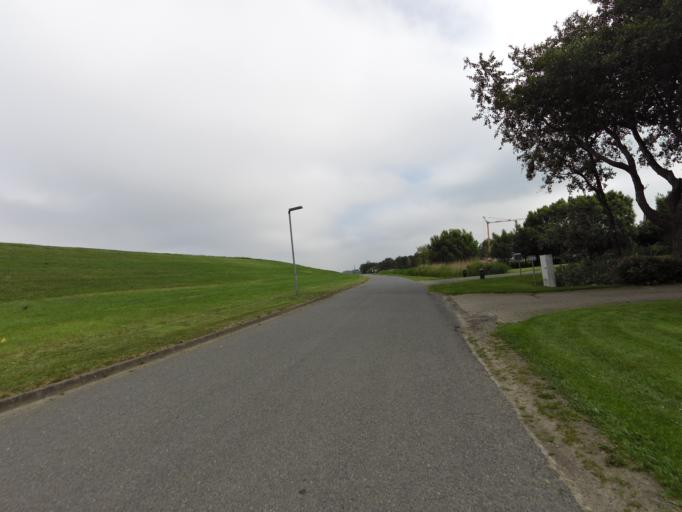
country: DE
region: Lower Saxony
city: Padingbuttel
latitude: 53.7436
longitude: 8.5261
